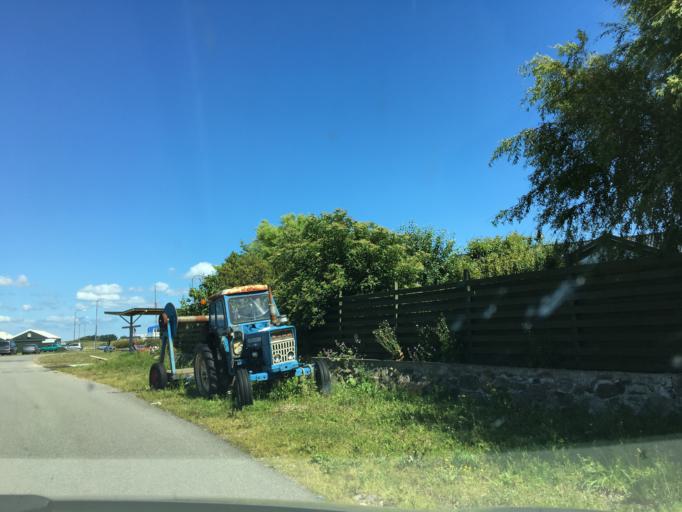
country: DK
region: South Denmark
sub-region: AEro Kommune
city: Marstal
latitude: 54.7501
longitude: 10.6738
